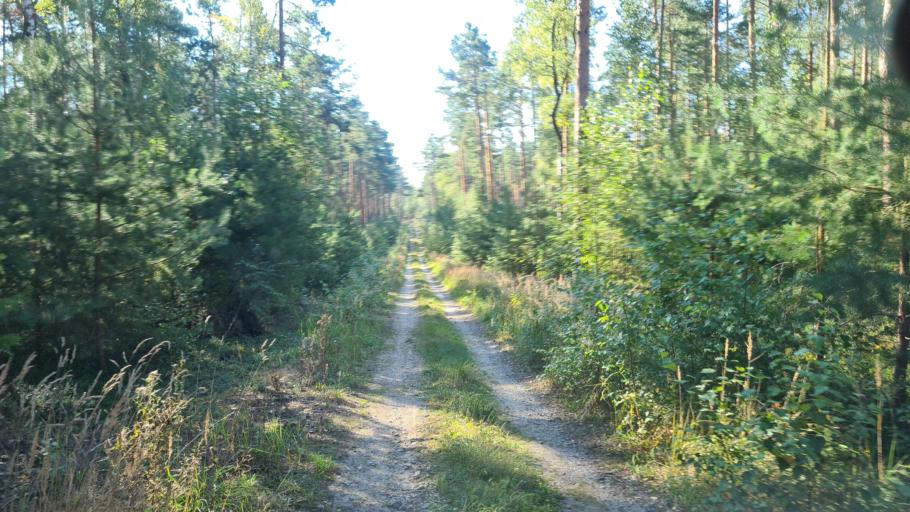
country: DE
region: Brandenburg
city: Schonborn
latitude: 51.6321
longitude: 13.5044
